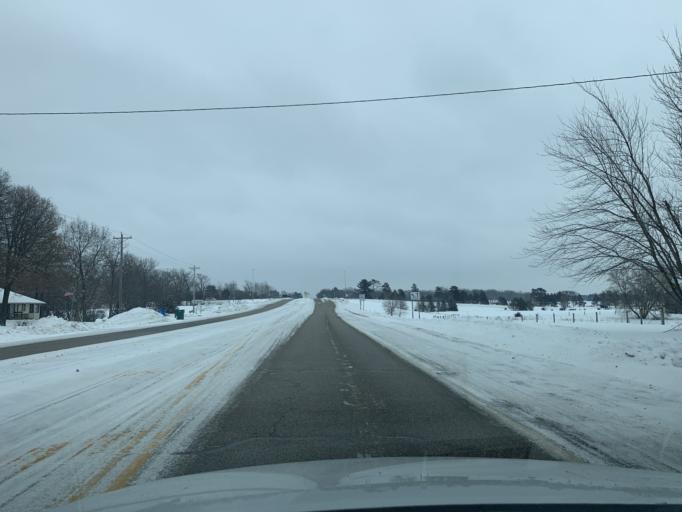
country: US
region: Minnesota
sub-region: Sherburne County
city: Zimmerman
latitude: 45.5016
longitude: -93.5872
